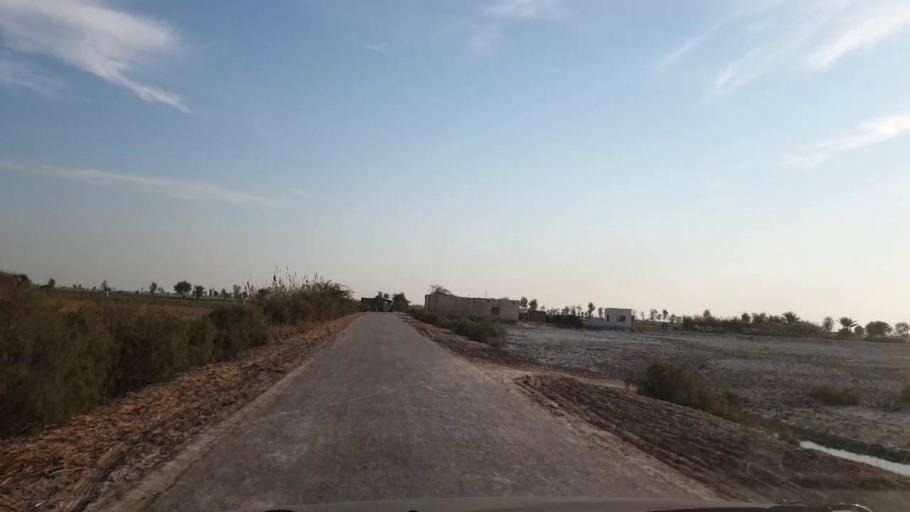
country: PK
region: Sindh
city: Khadro
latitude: 26.1611
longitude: 68.7534
